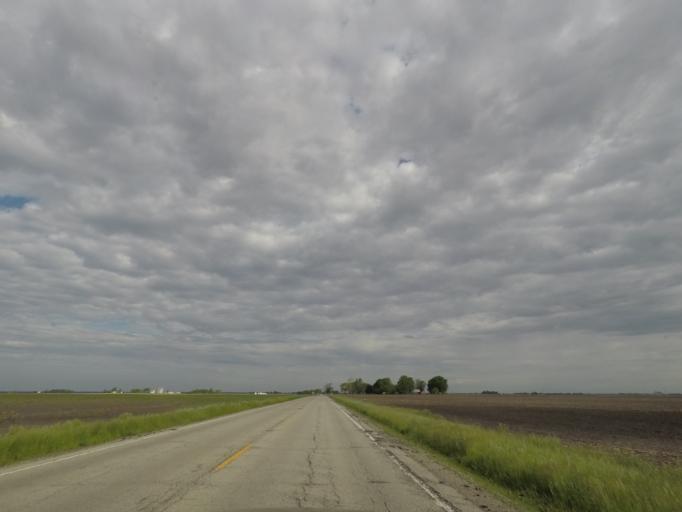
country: US
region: Illinois
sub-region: Logan County
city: Mount Pulaski
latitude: 40.0822
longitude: -89.3021
